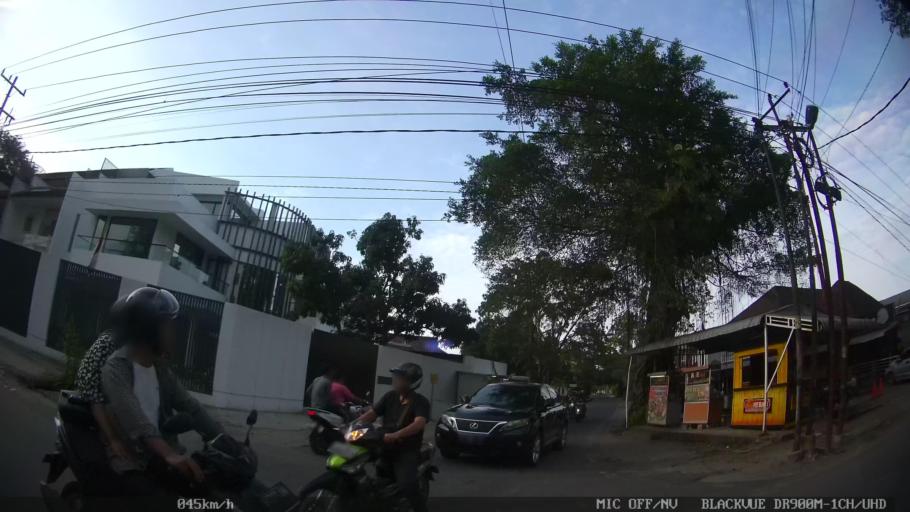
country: ID
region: North Sumatra
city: Medan
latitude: 3.5768
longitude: 98.6653
